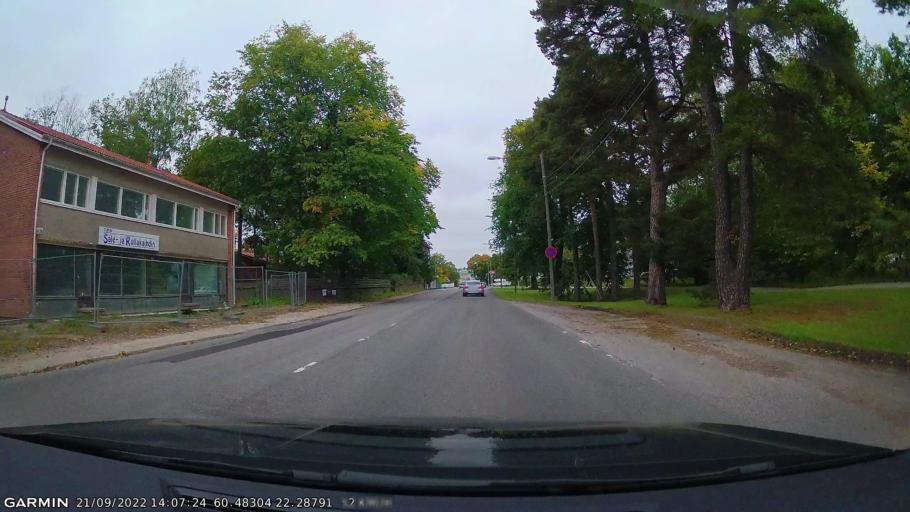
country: FI
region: Varsinais-Suomi
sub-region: Turku
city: Turku
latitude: 60.4832
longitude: 22.2878
